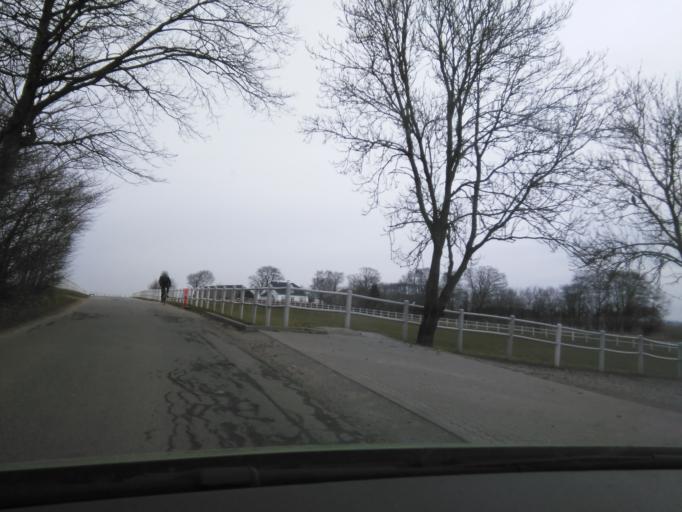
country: DK
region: Central Jutland
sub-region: Arhus Kommune
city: Marslet
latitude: 56.0951
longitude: 10.1773
